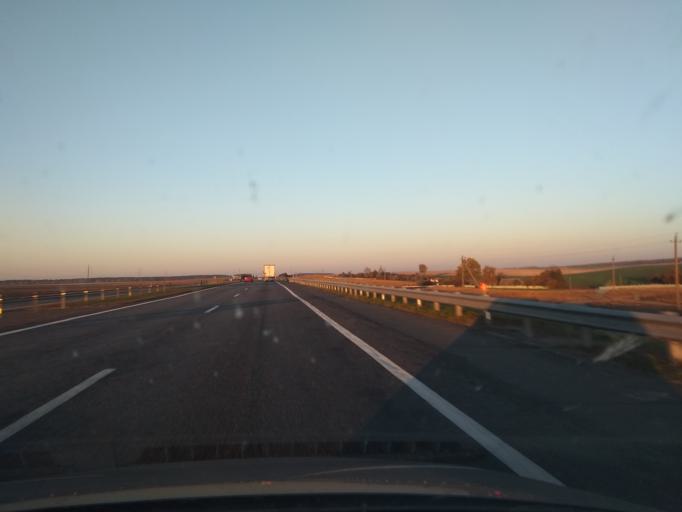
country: BY
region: Minsk
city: Haradzyeya
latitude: 53.3479
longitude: 26.4533
